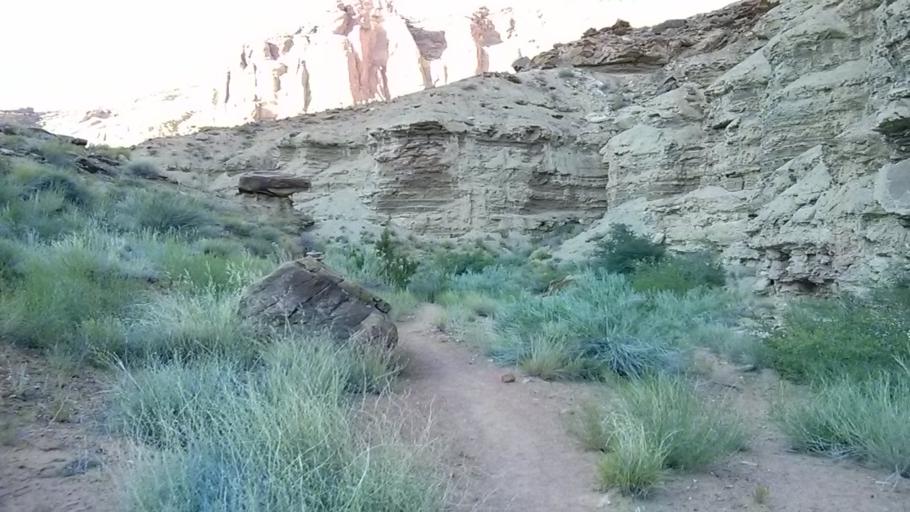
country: US
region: Utah
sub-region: Grand County
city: Moab
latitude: 38.4394
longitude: -109.9567
